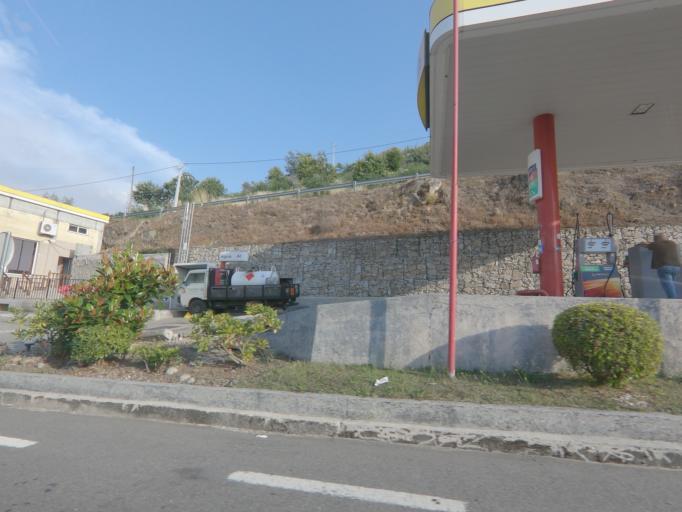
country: PT
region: Viseu
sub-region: Tabuaco
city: Tabuaco
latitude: 41.1160
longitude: -7.5754
